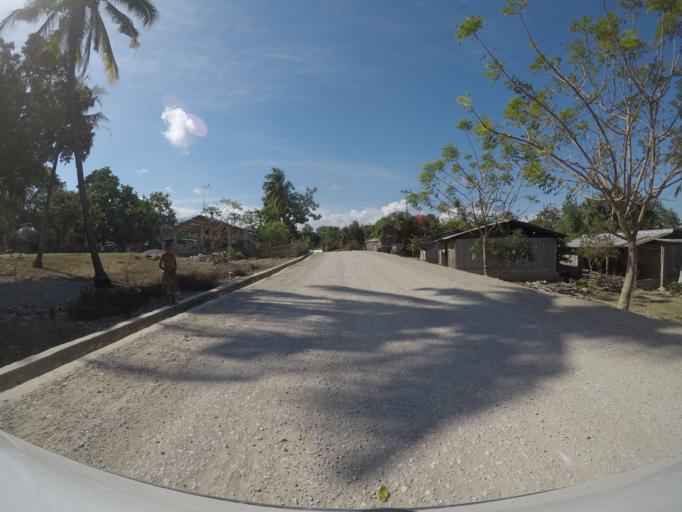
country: TL
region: Viqueque
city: Viqueque
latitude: -8.8411
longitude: 126.5165
